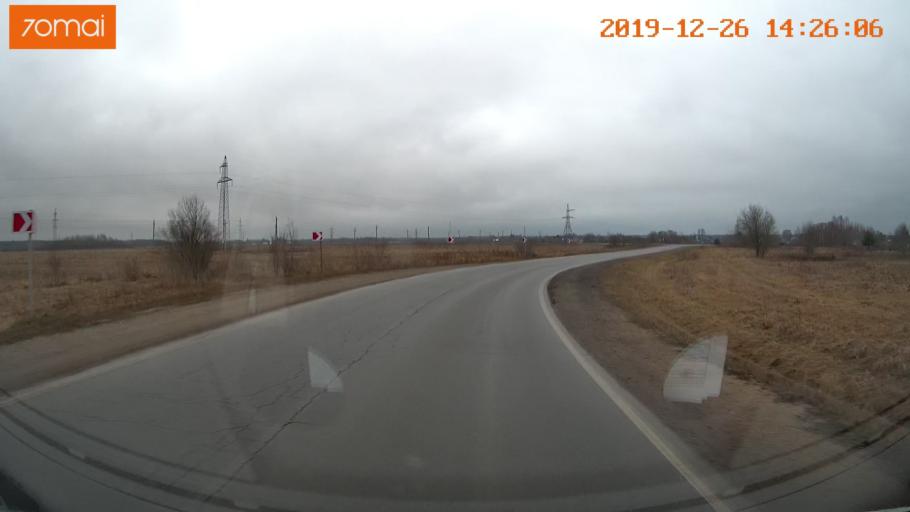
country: RU
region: Jaroslavl
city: Poshekhon'ye
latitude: 58.4888
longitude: 39.0915
